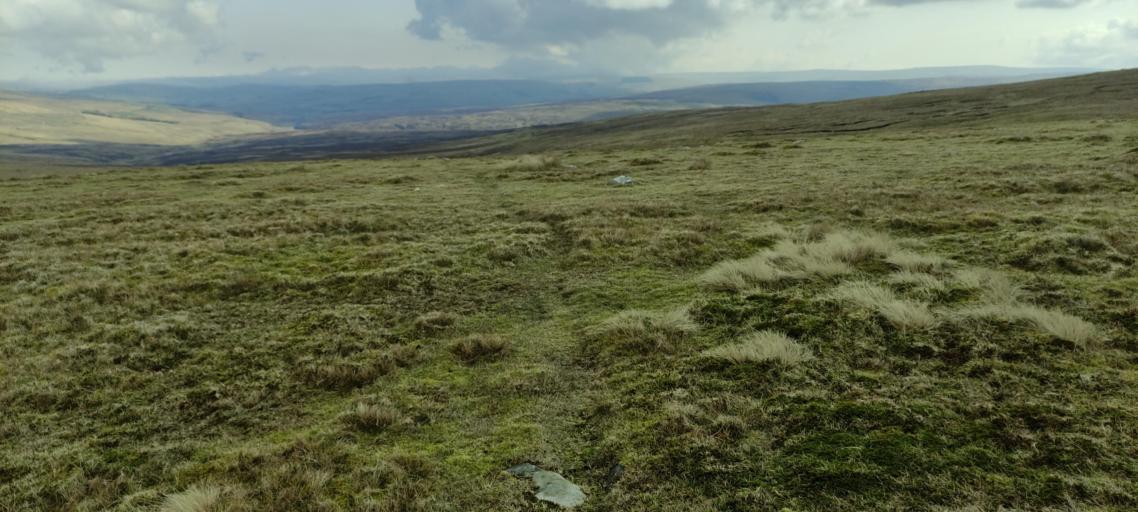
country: GB
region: England
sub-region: Cumbria
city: Appleby-in-Westmorland
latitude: 54.7402
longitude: -2.5510
